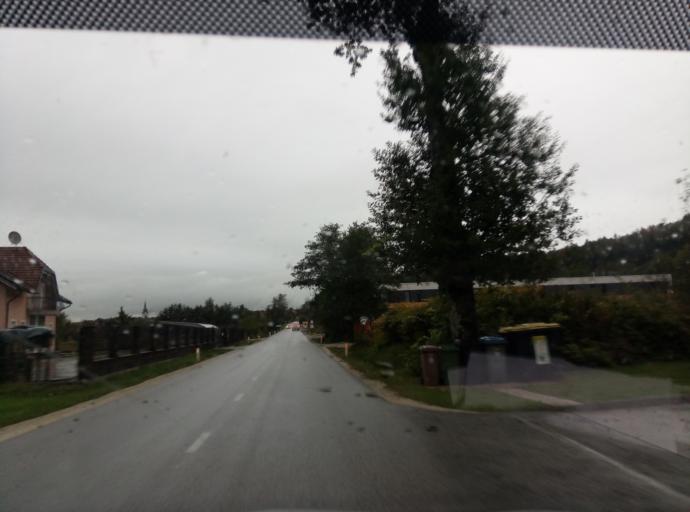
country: SI
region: Medvode
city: Zgornje Pirnice
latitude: 46.1312
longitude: 14.4777
